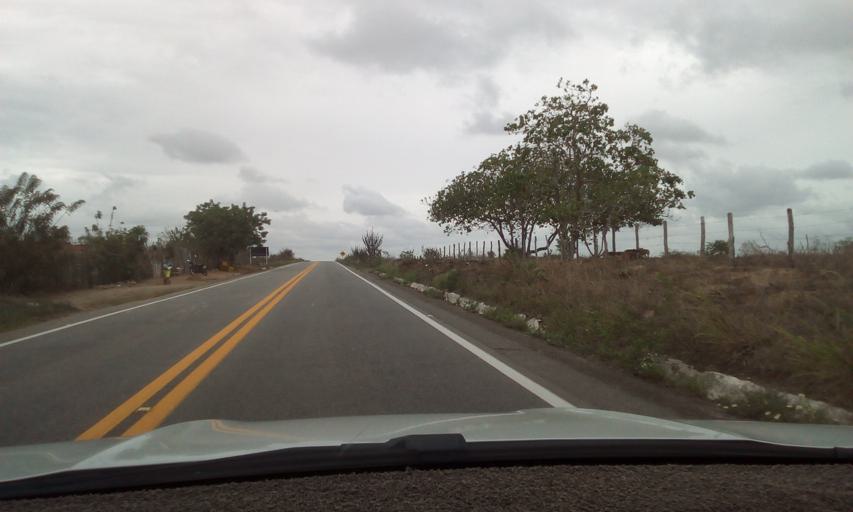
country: BR
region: Paraiba
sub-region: Areia
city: Remigio
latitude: -6.9183
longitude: -35.8509
